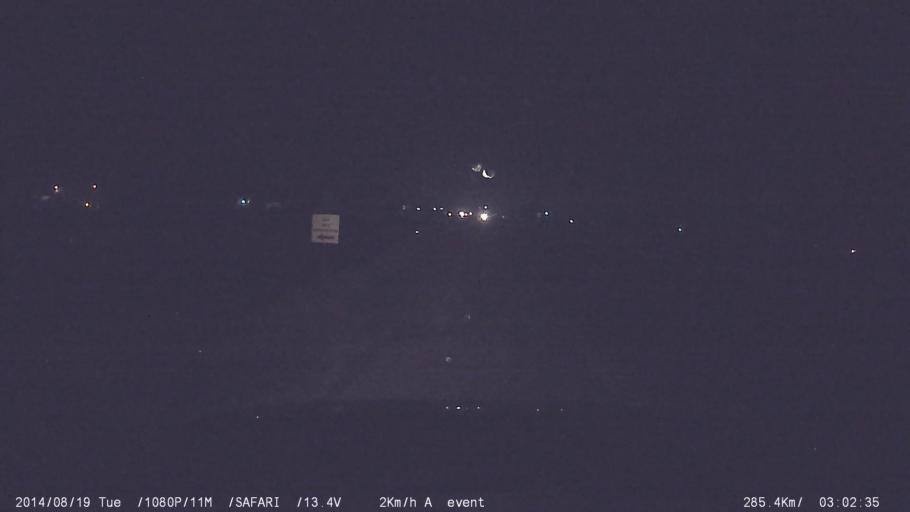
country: IN
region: Tamil Nadu
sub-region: Coimbatore
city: Sulur
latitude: 11.0741
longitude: 77.1092
